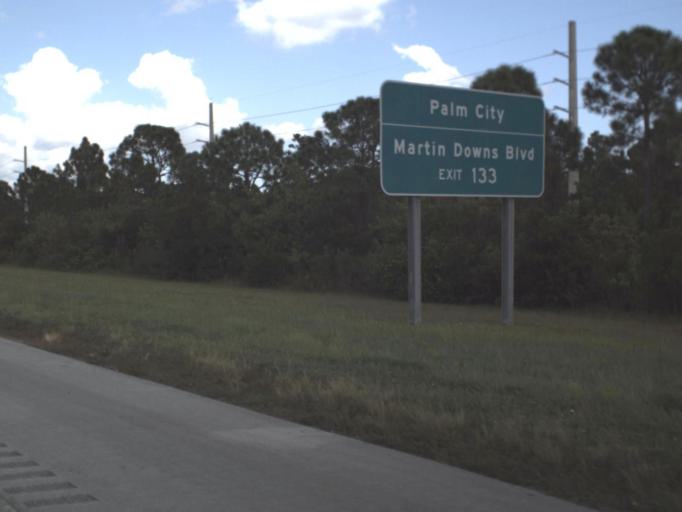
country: US
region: Florida
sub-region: Martin County
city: Palm City
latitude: 27.1360
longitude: -80.2873
